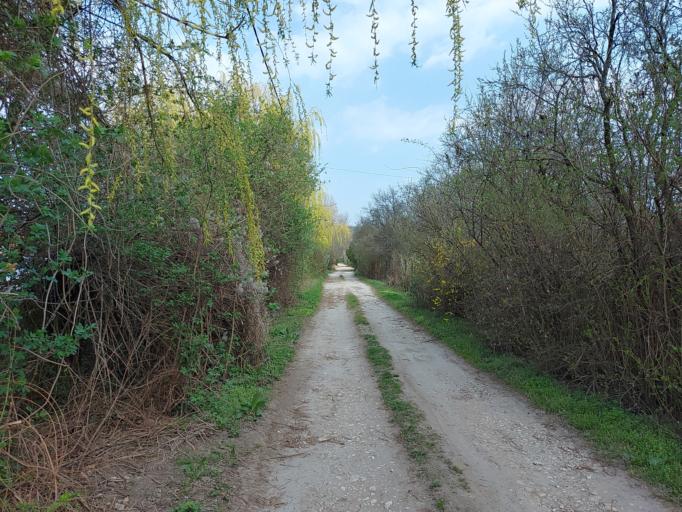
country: HU
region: Pest
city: Budaors
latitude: 47.4589
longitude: 18.9836
